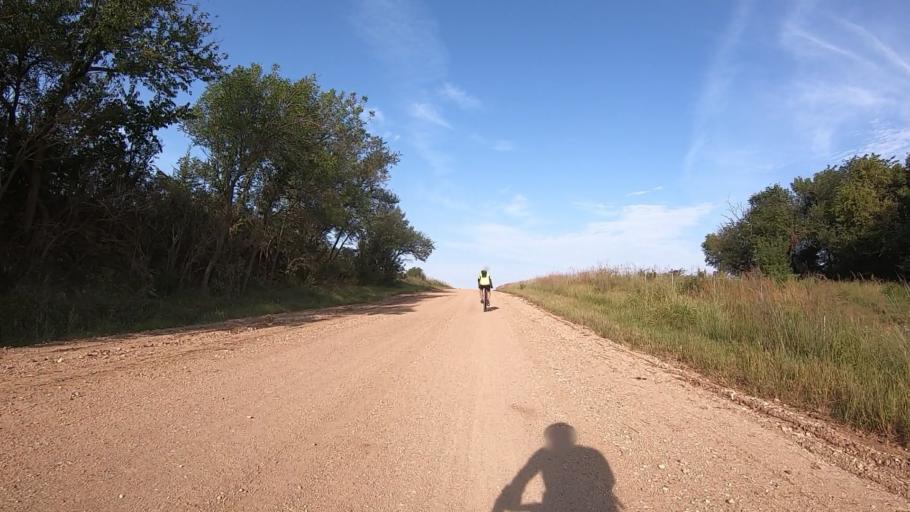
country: US
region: Kansas
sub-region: Marshall County
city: Blue Rapids
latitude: 39.6753
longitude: -96.7920
